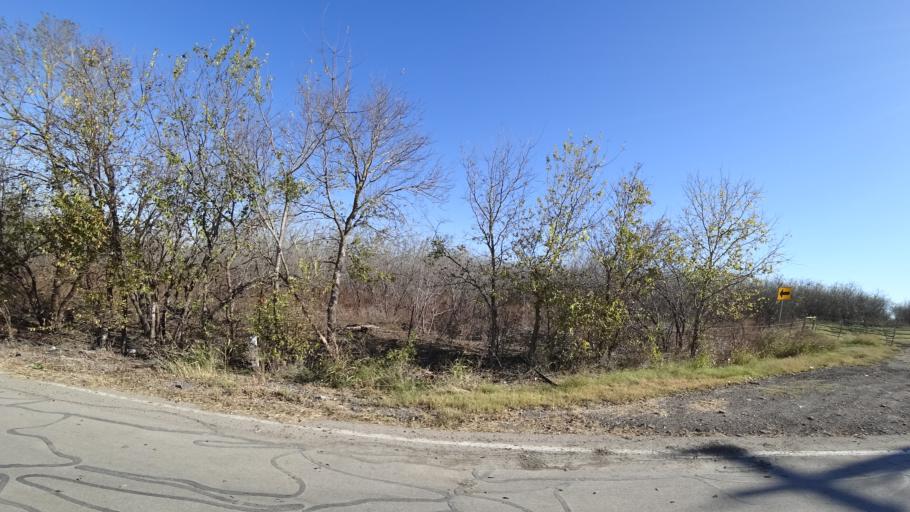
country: US
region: Texas
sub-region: Travis County
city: Onion Creek
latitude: 30.1113
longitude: -97.6699
